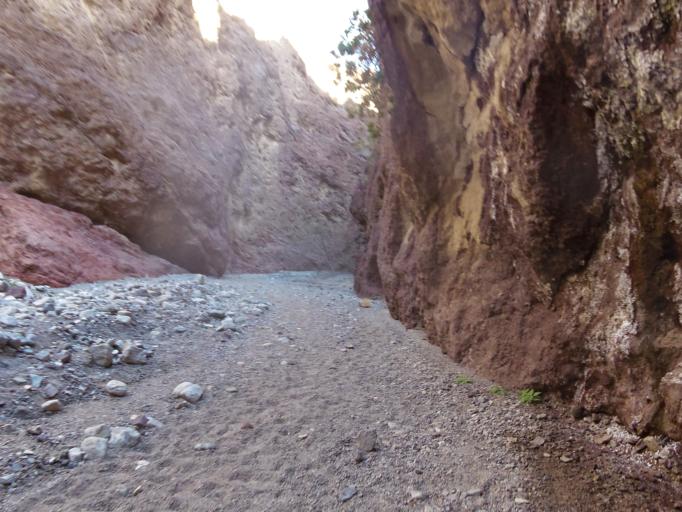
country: US
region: Nevada
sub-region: Clark County
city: Boulder City
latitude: 35.9650
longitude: -114.7263
